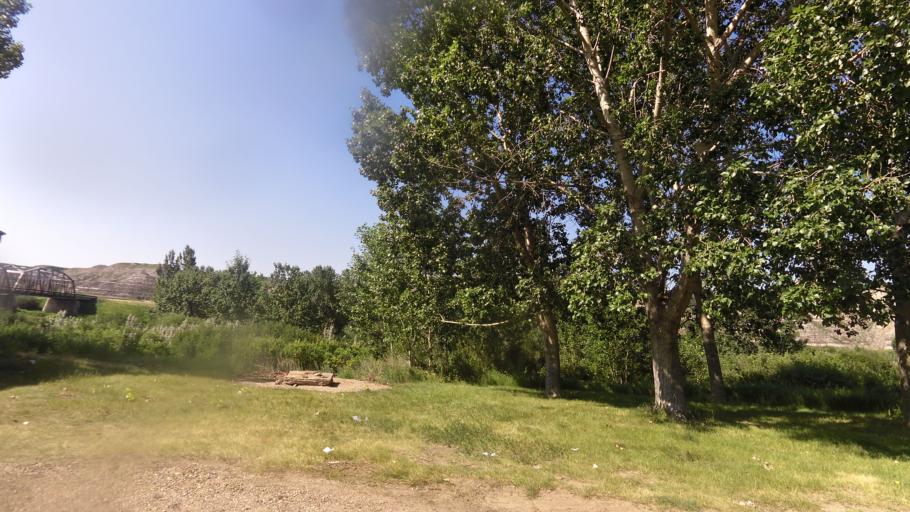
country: CA
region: Alberta
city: Three Hills
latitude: 51.6525
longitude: -112.9029
